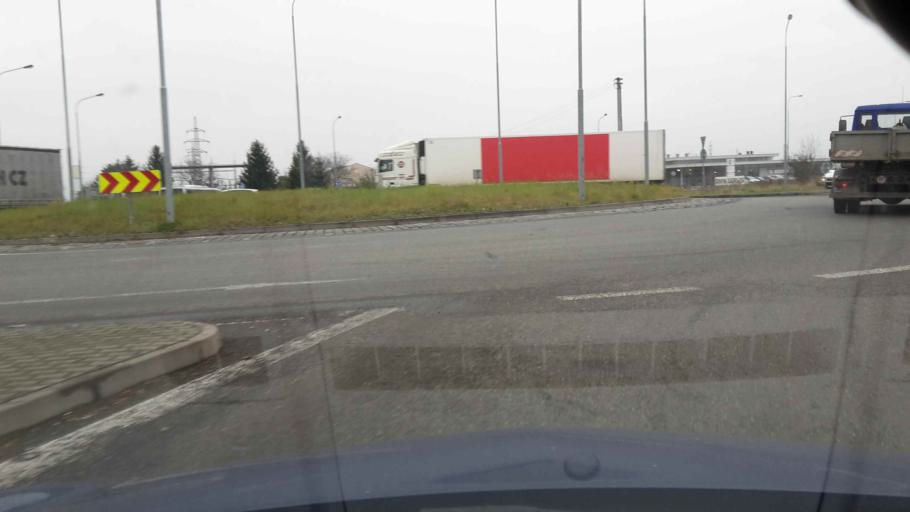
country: CZ
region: Olomoucky
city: Grygov
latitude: 49.5702
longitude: 17.3008
